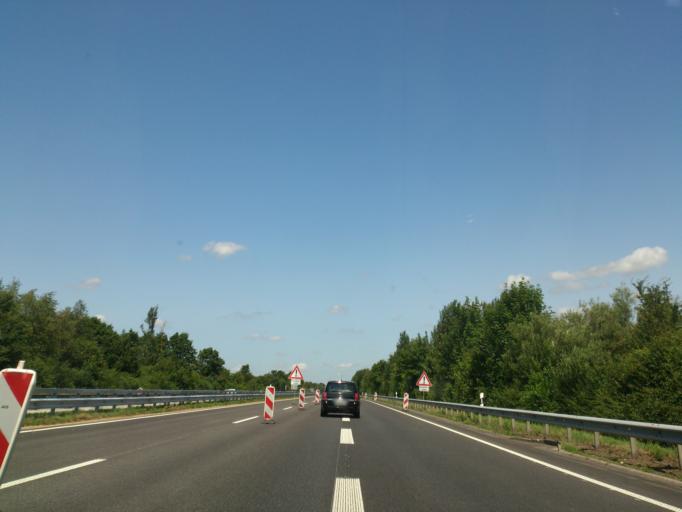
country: DE
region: Schleswig-Holstein
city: Tensbuttel-Rost
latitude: 54.1212
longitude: 9.2578
